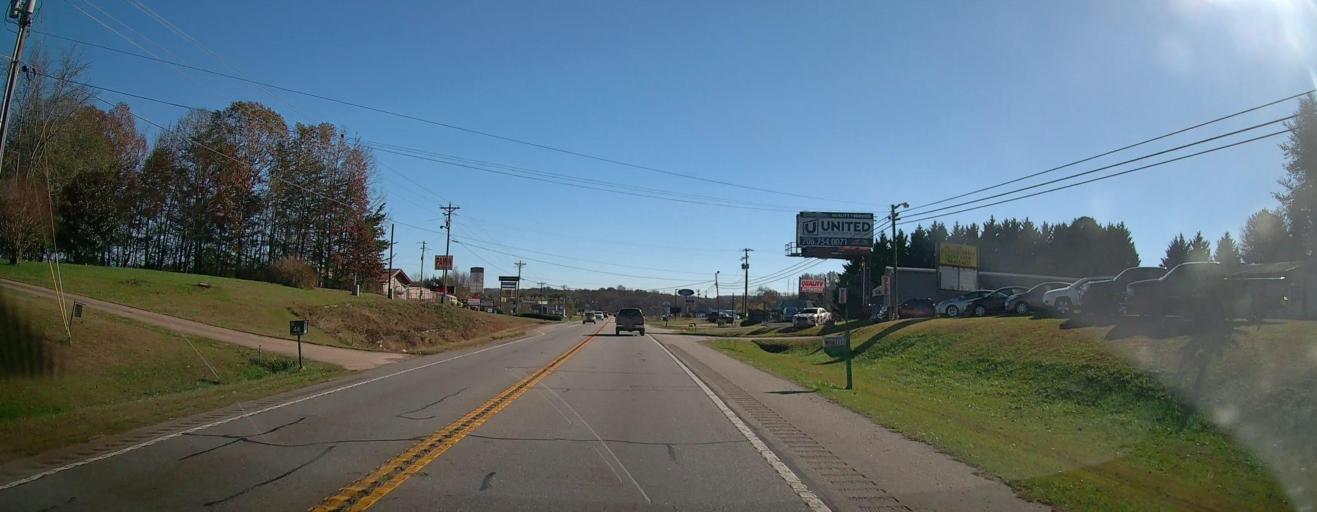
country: US
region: Georgia
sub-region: White County
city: Cleveland
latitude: 34.5611
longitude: -83.7630
